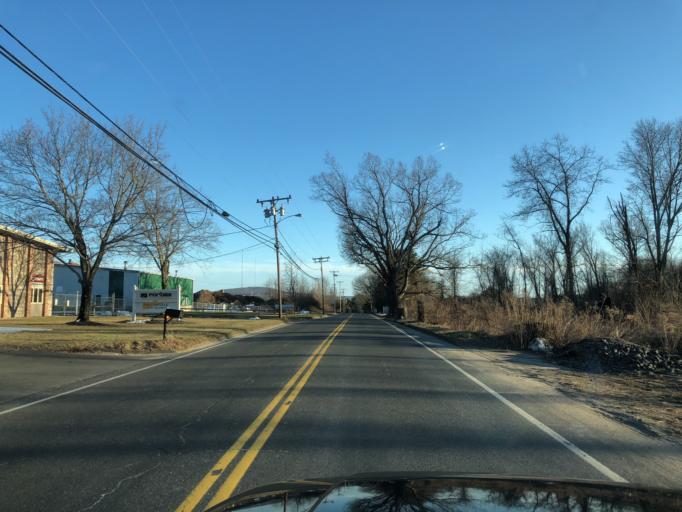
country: US
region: Connecticut
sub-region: Hartford County
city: Farmington
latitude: 41.7512
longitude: -72.8553
